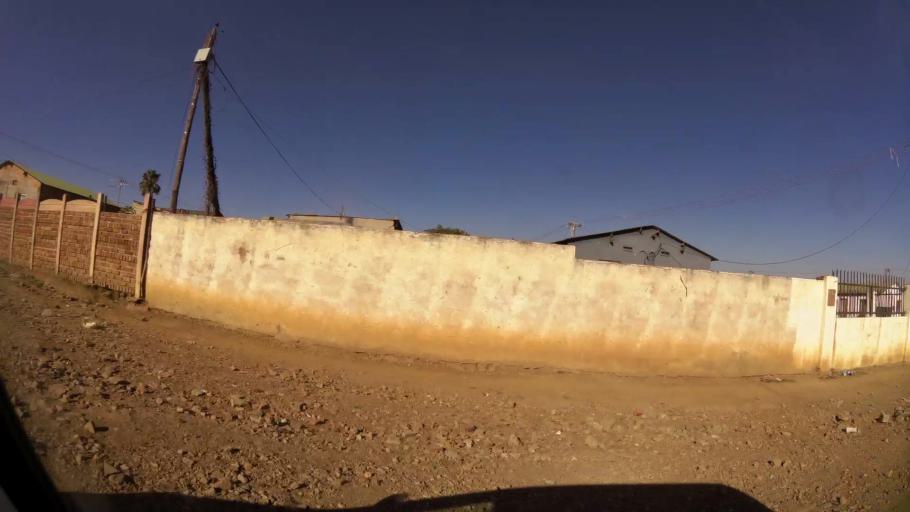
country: ZA
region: Gauteng
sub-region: City of Tshwane Metropolitan Municipality
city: Cullinan
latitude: -25.7192
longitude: 28.3866
